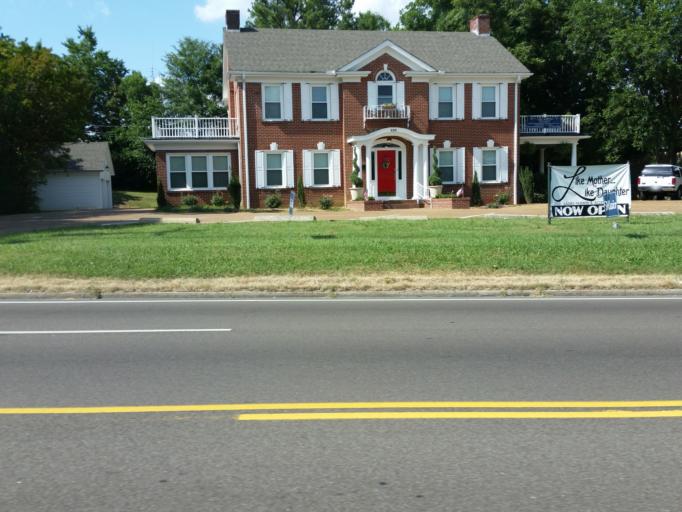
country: US
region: Tennessee
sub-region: Henderson County
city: Lexington
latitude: 35.6542
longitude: -88.3991
